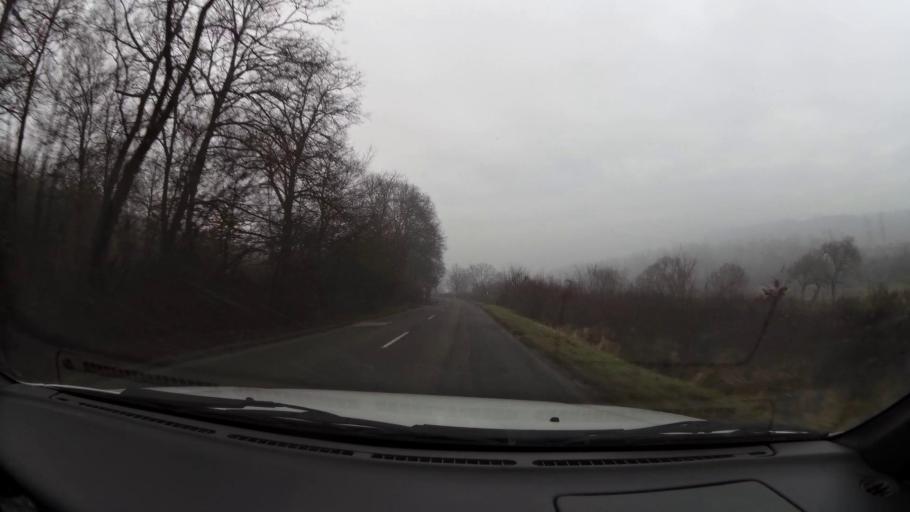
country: HU
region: Borsod-Abauj-Zemplen
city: Rudabanya
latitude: 48.3564
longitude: 20.6346
